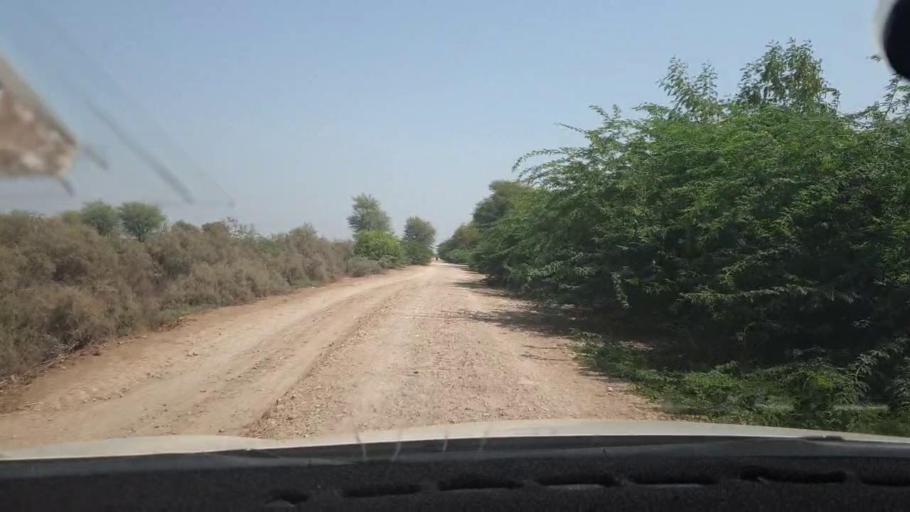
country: PK
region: Sindh
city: Tando Mittha Khan
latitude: 25.9166
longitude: 69.2397
